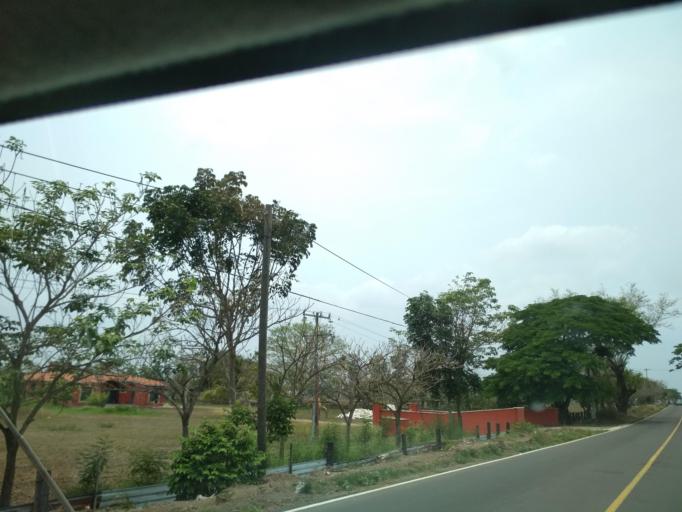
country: MX
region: Veracruz
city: Manlio Fabio Altamirano
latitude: 19.1357
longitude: -96.2984
